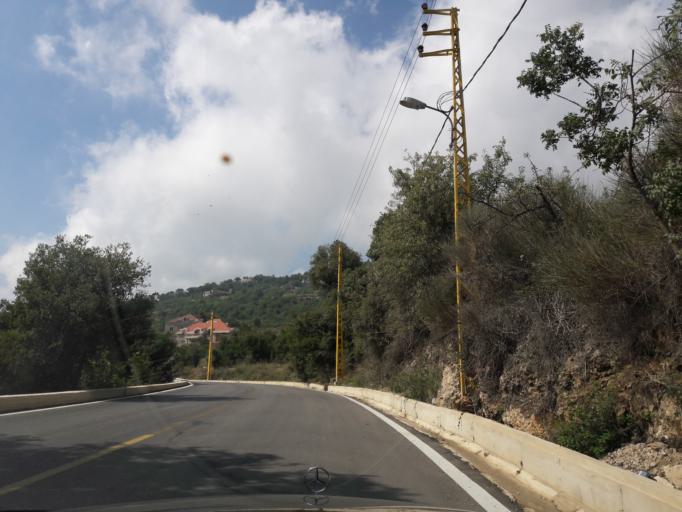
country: LB
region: Mont-Liban
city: Djounie
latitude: 33.9639
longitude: 35.7743
